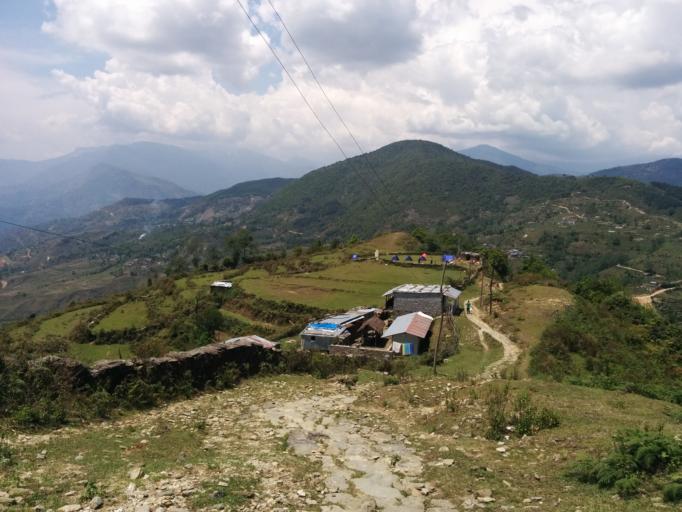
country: NP
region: Western Region
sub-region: Gandaki Zone
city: Pokhara
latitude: 28.2589
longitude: 83.8212
